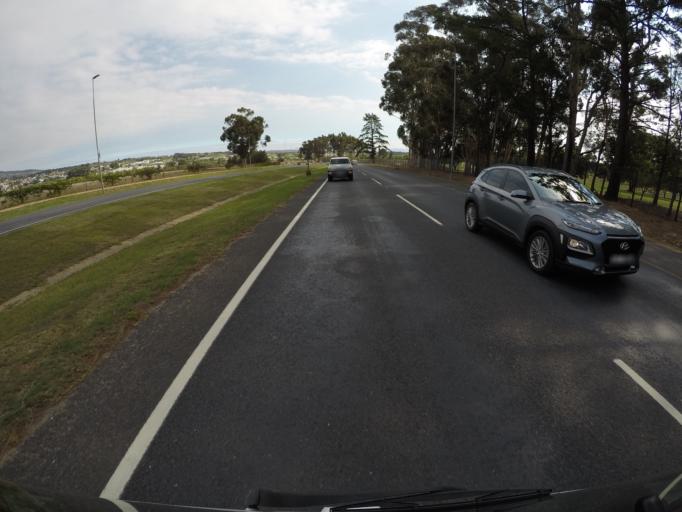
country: ZA
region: Western Cape
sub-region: Cape Winelands District Municipality
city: Stellenbosch
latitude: -33.9648
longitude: 18.8478
